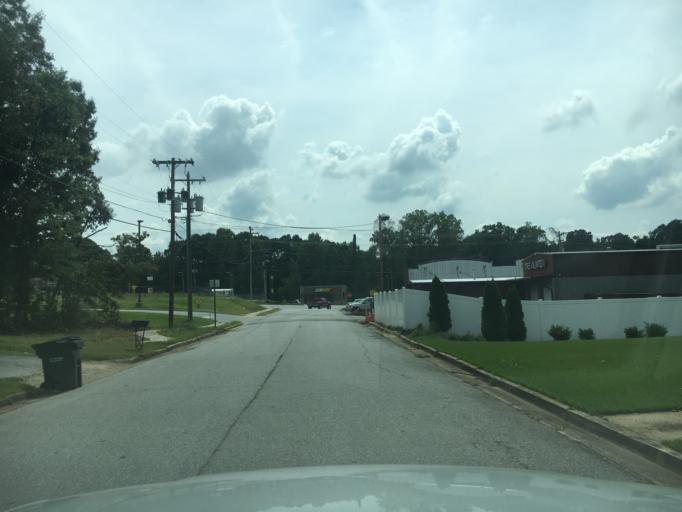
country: US
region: South Carolina
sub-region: Greenville County
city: Greer
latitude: 34.9494
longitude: -82.2278
